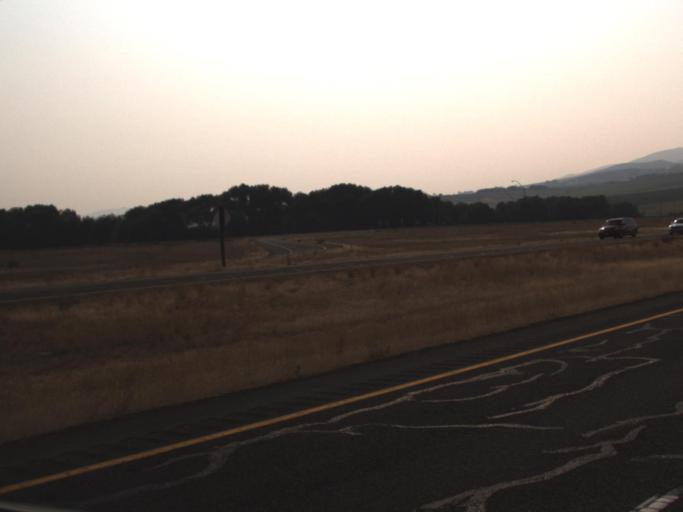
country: US
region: Washington
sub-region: Kittitas County
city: Ellensburg
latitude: 46.9302
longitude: -120.5019
